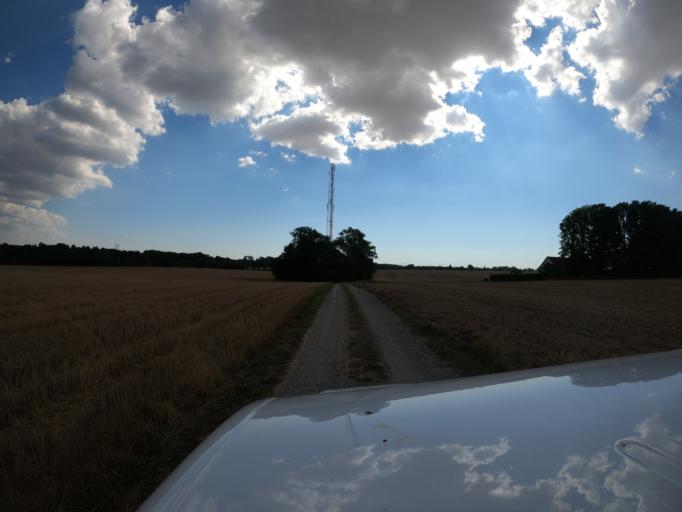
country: SE
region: Skane
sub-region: Lunds Kommun
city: Lund
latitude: 55.7091
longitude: 13.3195
